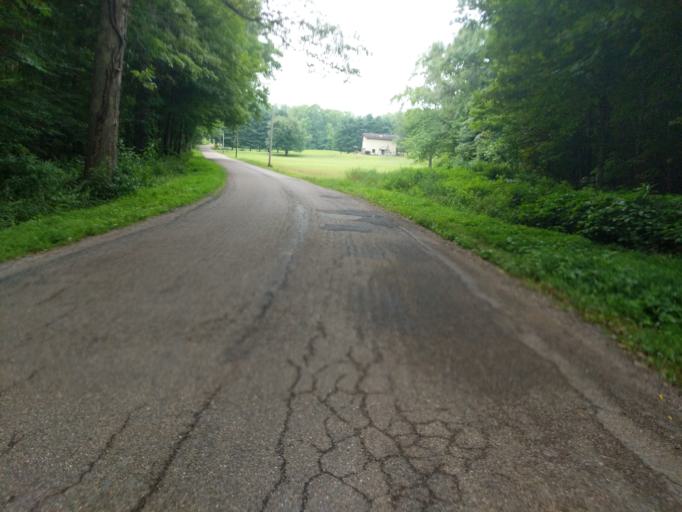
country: US
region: Ohio
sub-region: Athens County
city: The Plains
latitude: 39.3796
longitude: -82.1443
